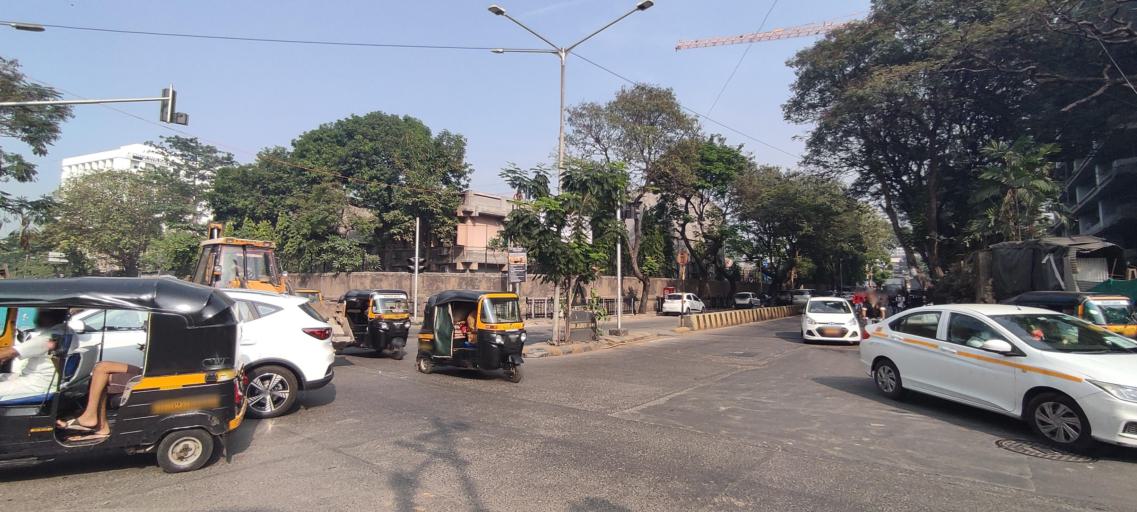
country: IN
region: Maharashtra
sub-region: Mumbai Suburban
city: Mumbai
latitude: 19.1084
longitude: 72.8369
